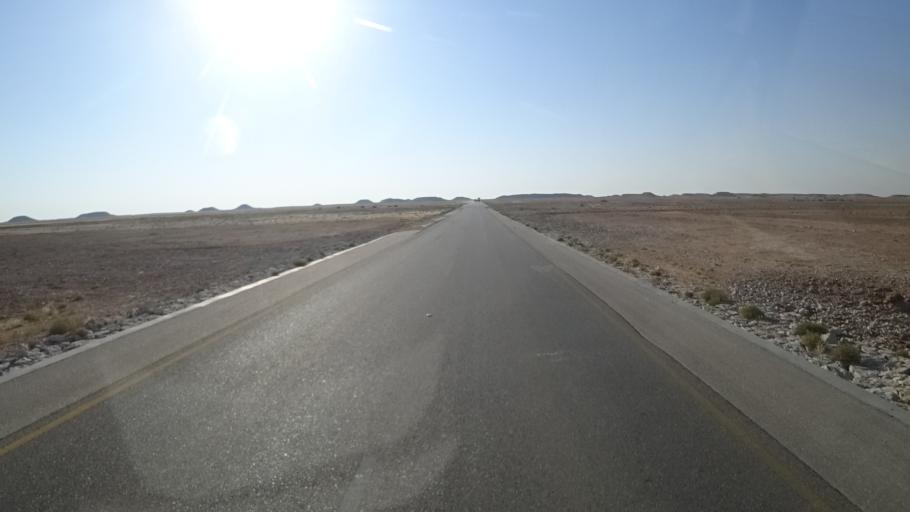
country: OM
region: Zufar
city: Salalah
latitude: 17.6417
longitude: 53.8264
